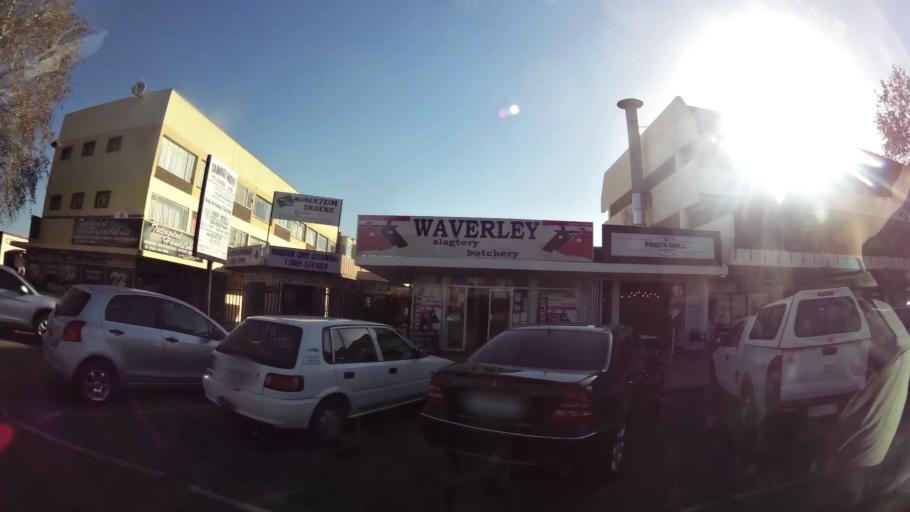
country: ZA
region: Gauteng
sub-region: City of Tshwane Metropolitan Municipality
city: Pretoria
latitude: -25.7031
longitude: 28.2427
